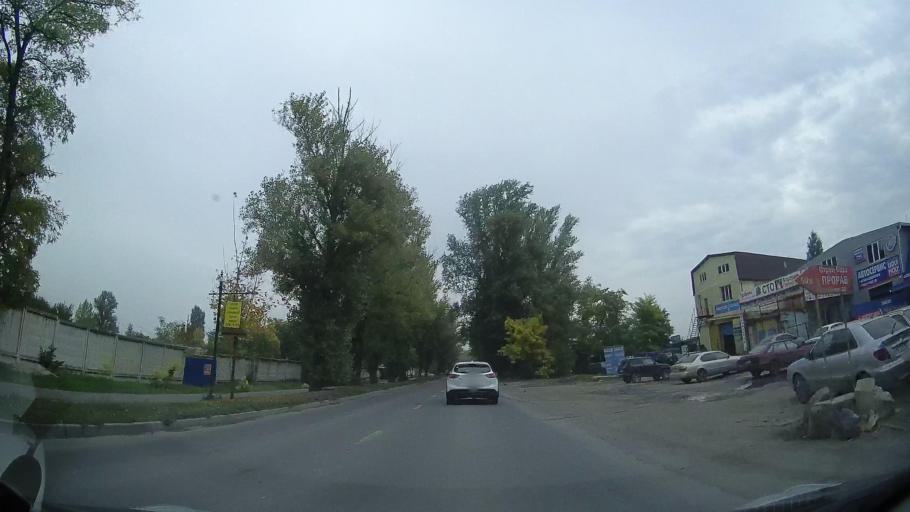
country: RU
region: Rostov
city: Severnyy
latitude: 47.2805
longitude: 39.6632
